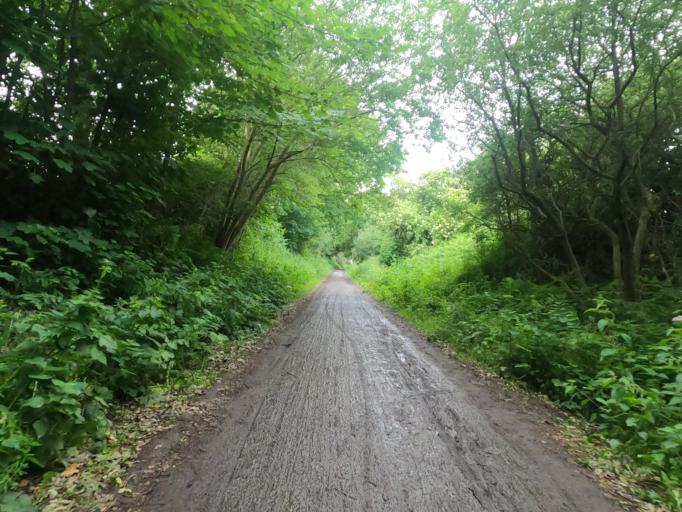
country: GB
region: England
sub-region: Cheshire West and Chester
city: Over
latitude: 53.2044
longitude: -2.5567
